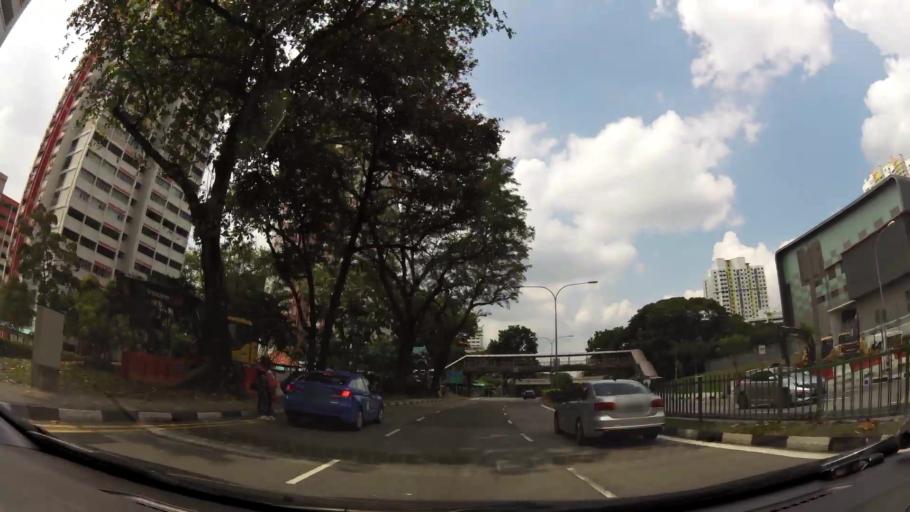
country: SG
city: Singapore
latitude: 1.2782
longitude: 103.8305
